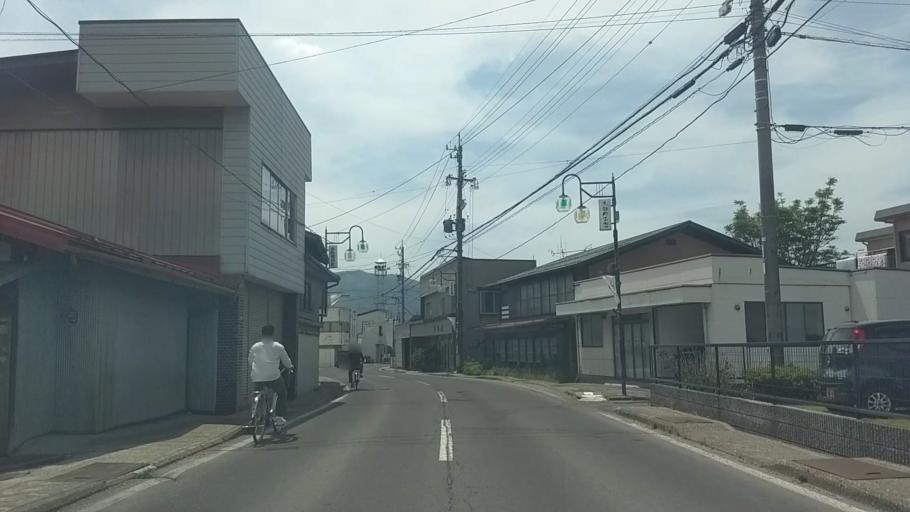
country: JP
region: Nagano
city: Chino
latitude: 35.9974
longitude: 138.1689
